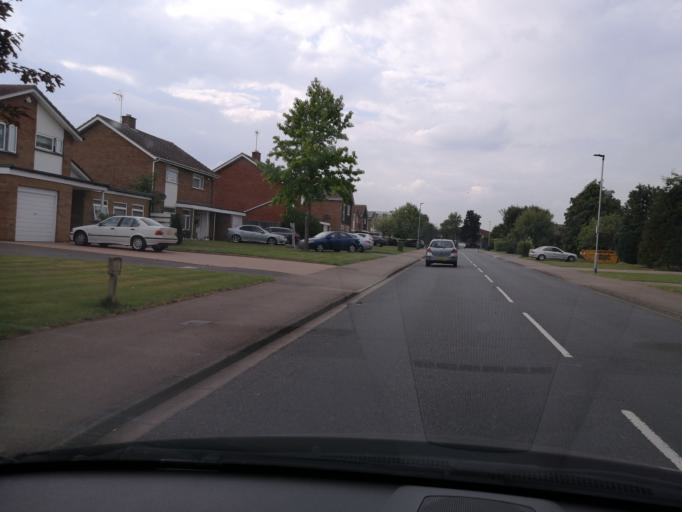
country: GB
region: England
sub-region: Peterborough
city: Peterborough
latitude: 52.5778
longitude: -0.2742
